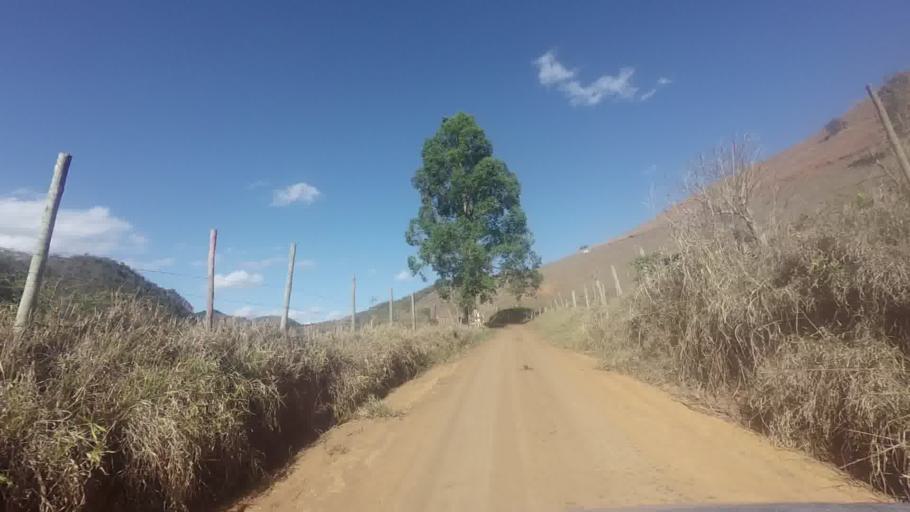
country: BR
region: Espirito Santo
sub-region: Sao Jose Do Calcado
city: Sao Jose do Calcado
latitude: -21.0305
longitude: -41.5889
